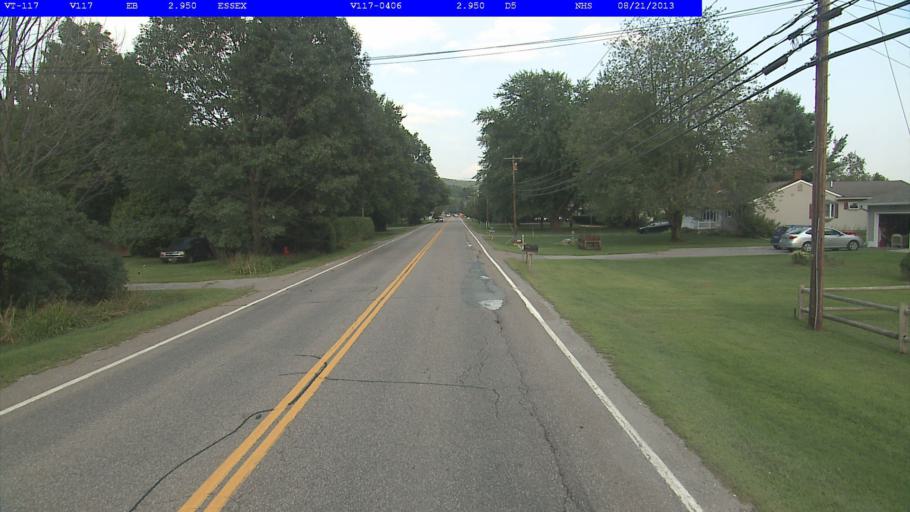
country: US
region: Vermont
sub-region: Chittenden County
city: Williston
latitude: 44.4790
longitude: -73.0559
